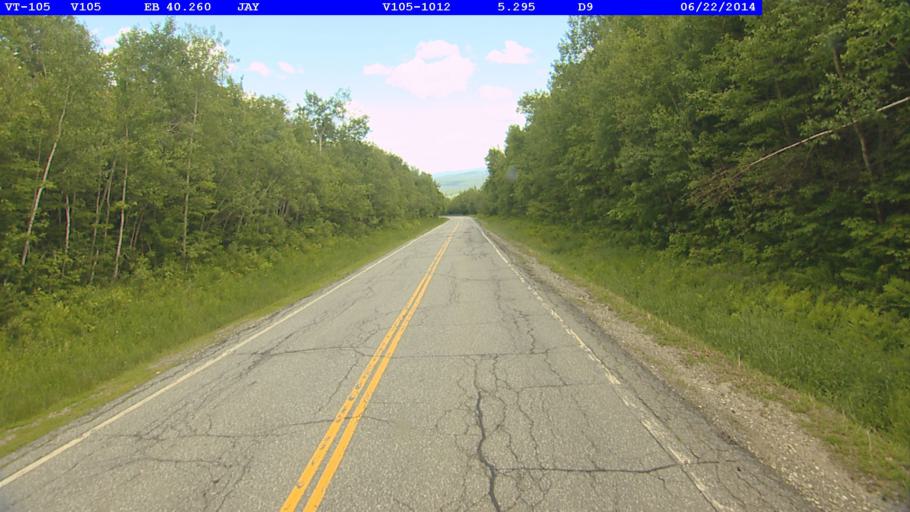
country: CA
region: Quebec
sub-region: Monteregie
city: Sutton
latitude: 44.9784
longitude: -72.4797
